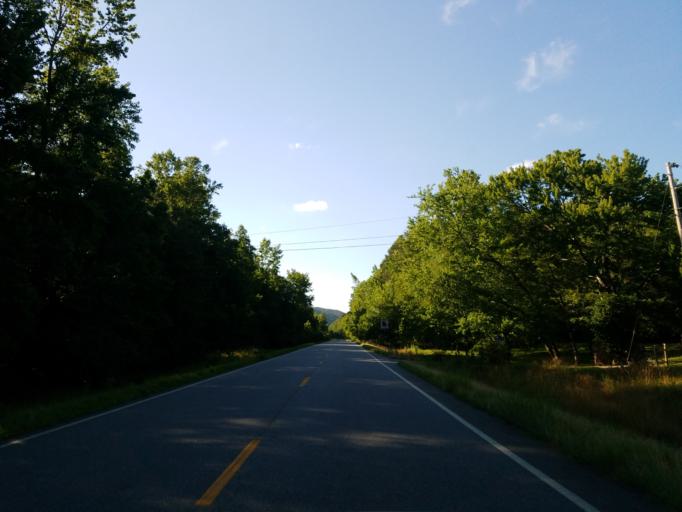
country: US
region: Georgia
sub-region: Gordon County
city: Calhoun
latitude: 34.6275
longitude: -85.0570
